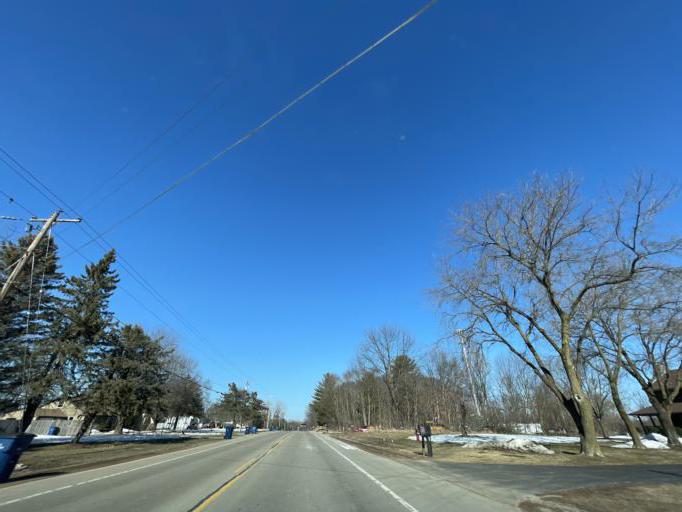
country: US
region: Wisconsin
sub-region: Brown County
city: Suamico
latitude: 44.6126
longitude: -88.0709
